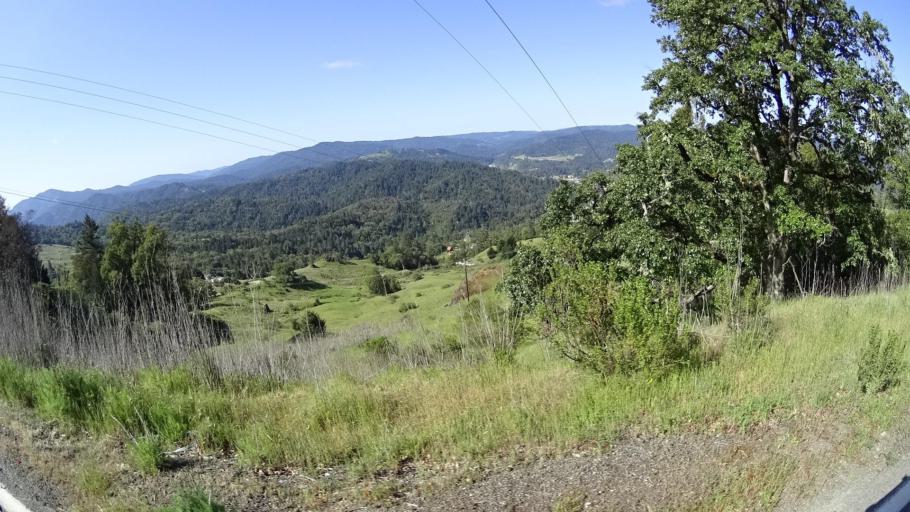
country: US
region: California
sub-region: Humboldt County
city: Redway
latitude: 40.1117
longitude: -123.7704
